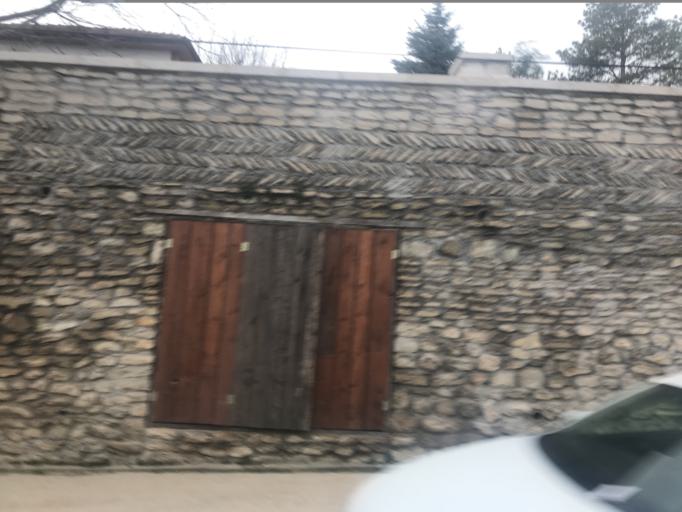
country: TR
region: Karabuk
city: Safranbolu
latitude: 41.2599
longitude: 32.6789
